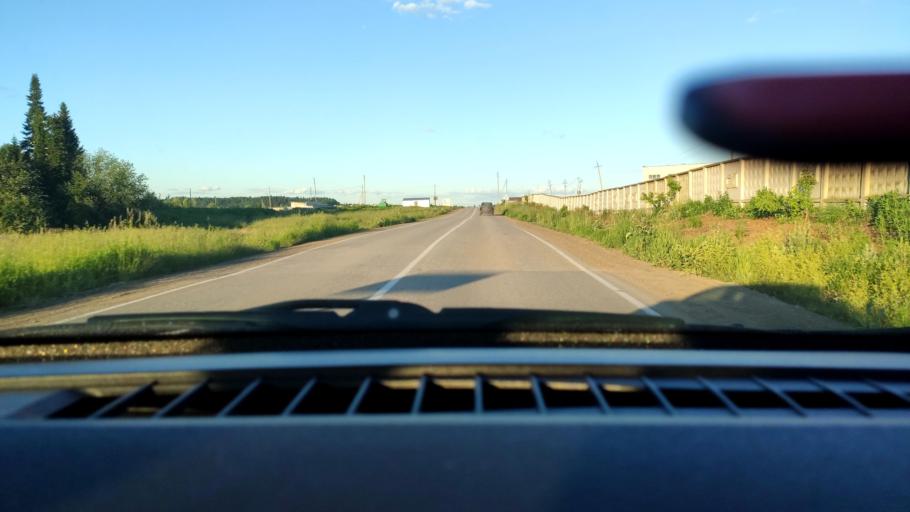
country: RU
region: Perm
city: Kultayevo
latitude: 57.9242
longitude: 55.9049
